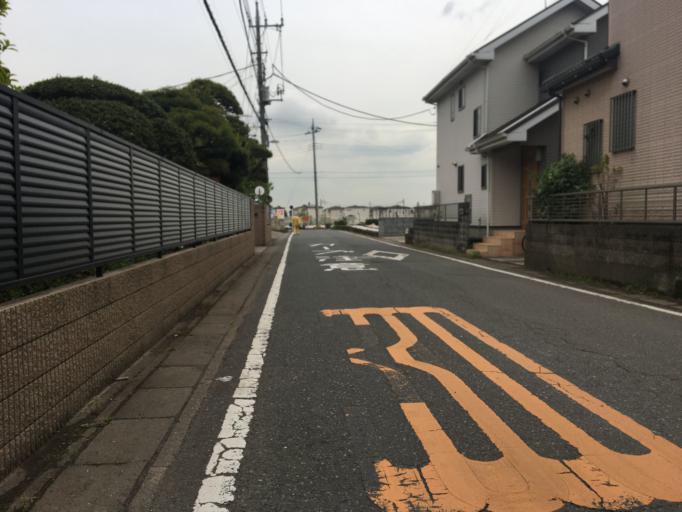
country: JP
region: Saitama
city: Oi
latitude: 35.8526
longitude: 139.5465
